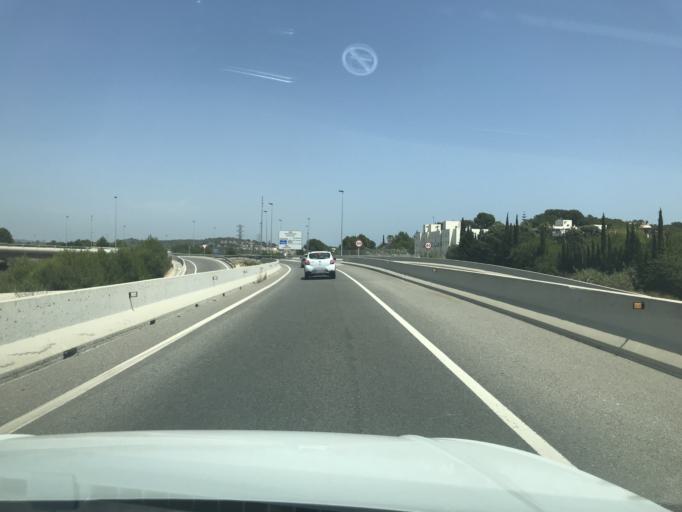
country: ES
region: Catalonia
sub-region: Provincia de Tarragona
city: Altafulla
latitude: 41.1379
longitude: 1.3438
